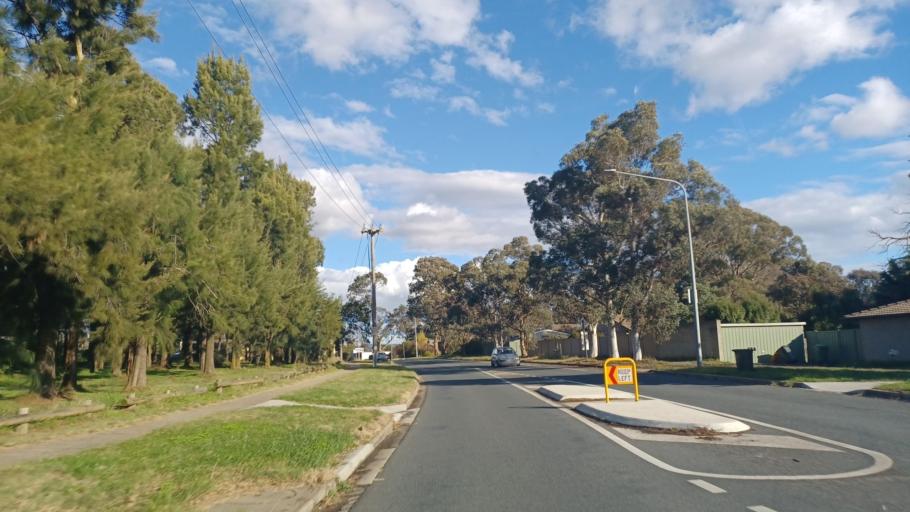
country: AU
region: Australian Capital Territory
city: Belconnen
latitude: -35.1941
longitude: 149.0418
